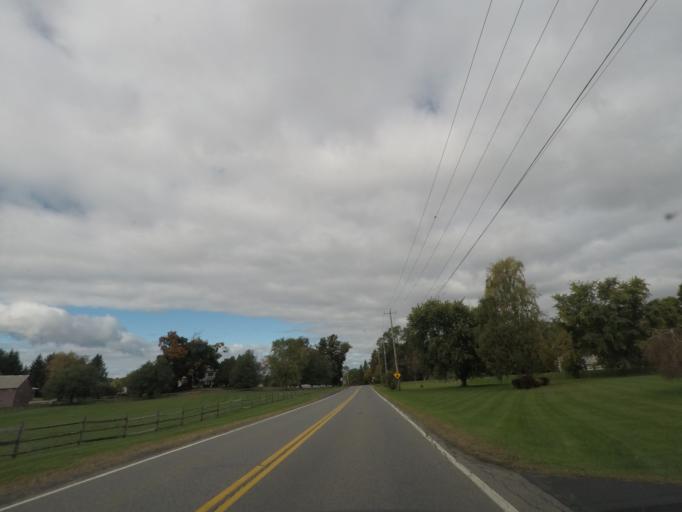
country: US
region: New York
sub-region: Saratoga County
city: Country Knolls
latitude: 42.8850
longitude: -73.7617
